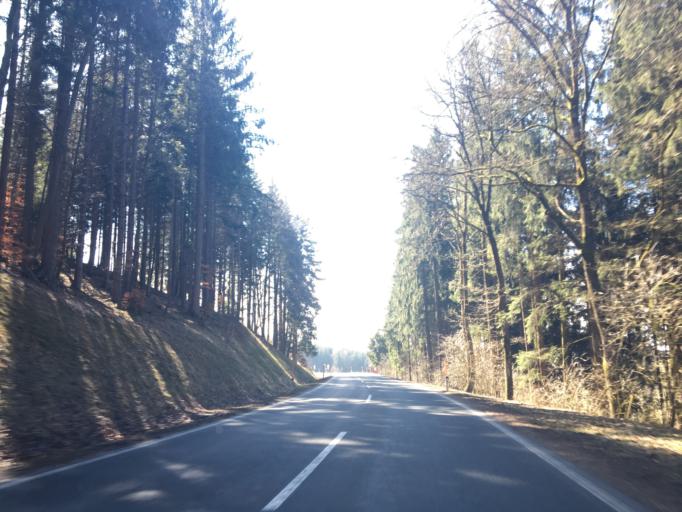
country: AT
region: Upper Austria
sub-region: Politischer Bezirk Perg
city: Sankt Georgen am Walde
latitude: 48.2925
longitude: 14.8987
